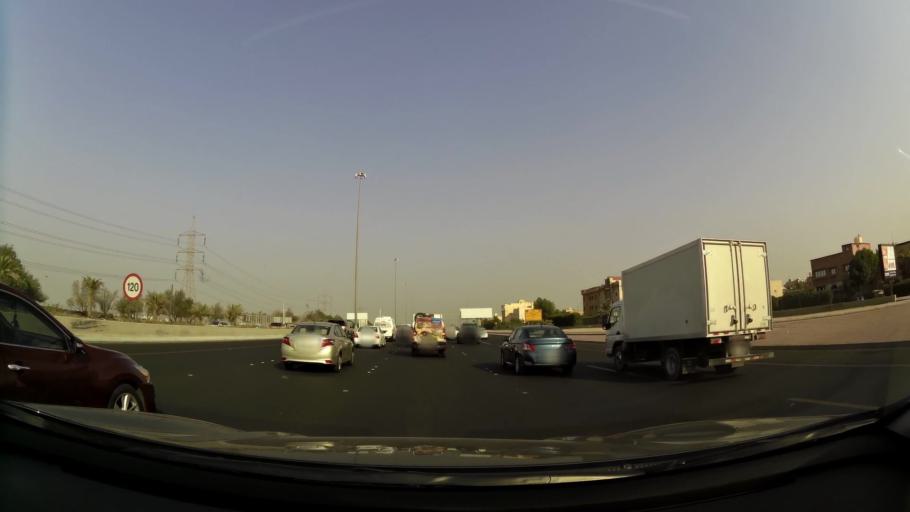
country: KW
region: Al Asimah
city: Ar Rabiyah
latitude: 29.3021
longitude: 47.9528
